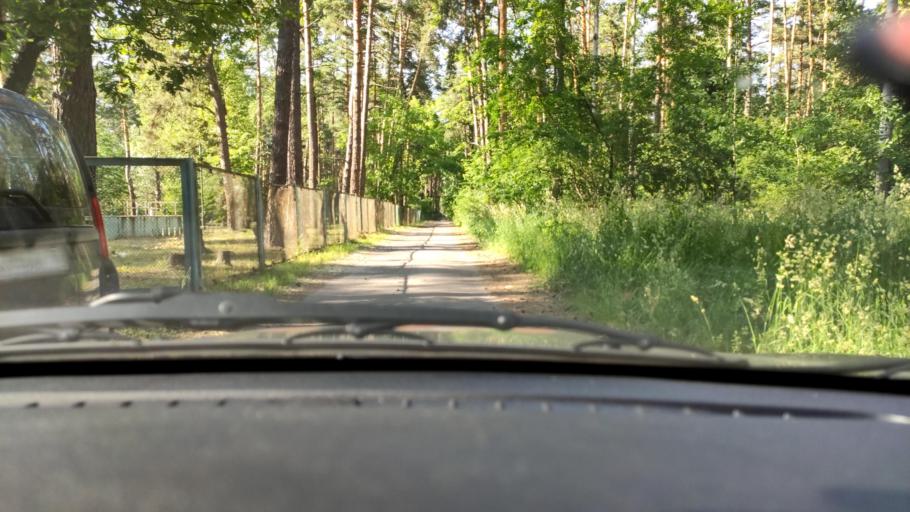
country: RU
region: Voronezj
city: Somovo
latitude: 51.7578
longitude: 39.3746
